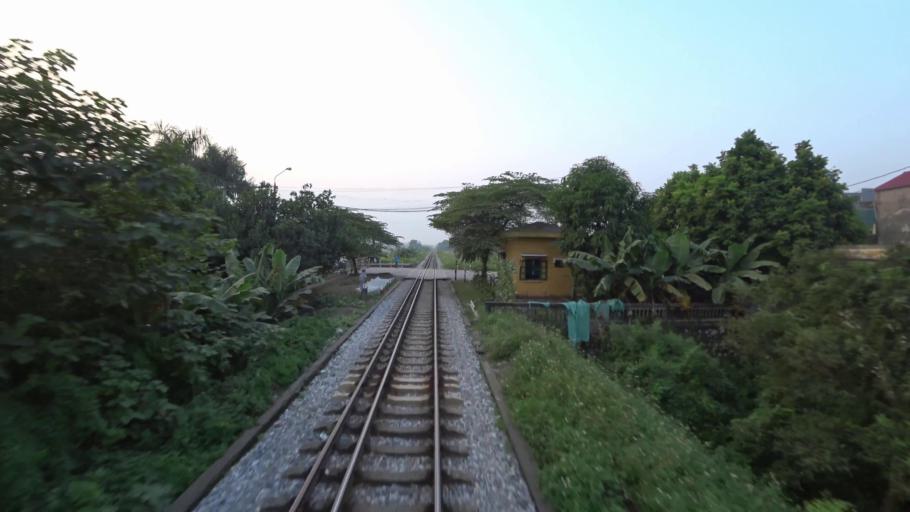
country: VN
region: Ha Noi
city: Dong Anh
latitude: 21.1268
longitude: 105.8797
